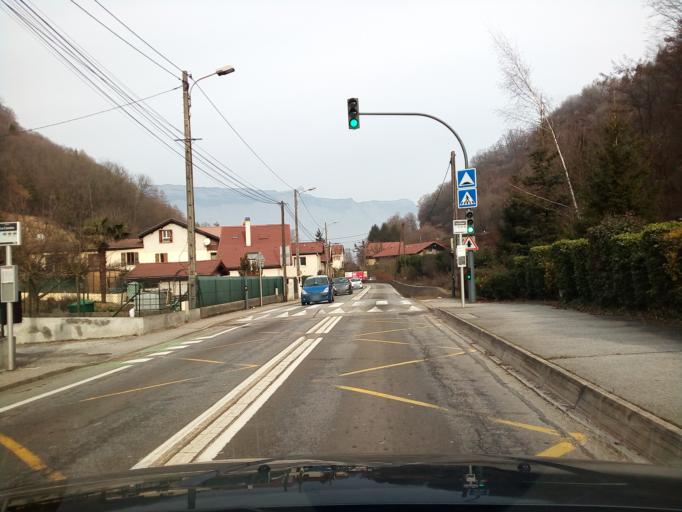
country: FR
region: Rhone-Alpes
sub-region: Departement de l'Isere
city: Gieres
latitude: 45.1740
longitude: 5.7900
